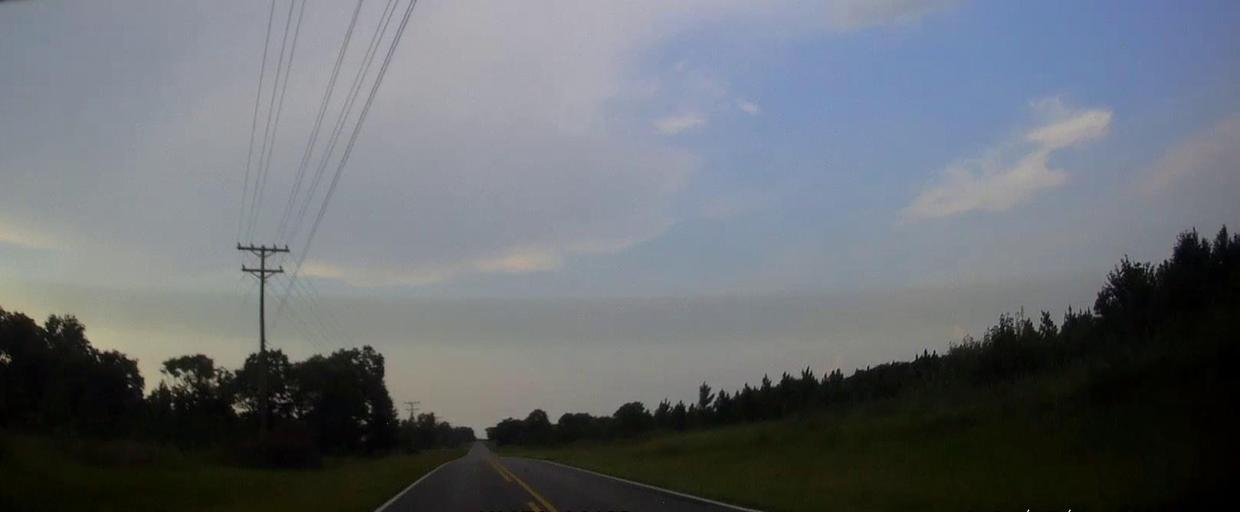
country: US
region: Georgia
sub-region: Laurens County
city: East Dublin
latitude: 32.5468
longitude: -82.8369
